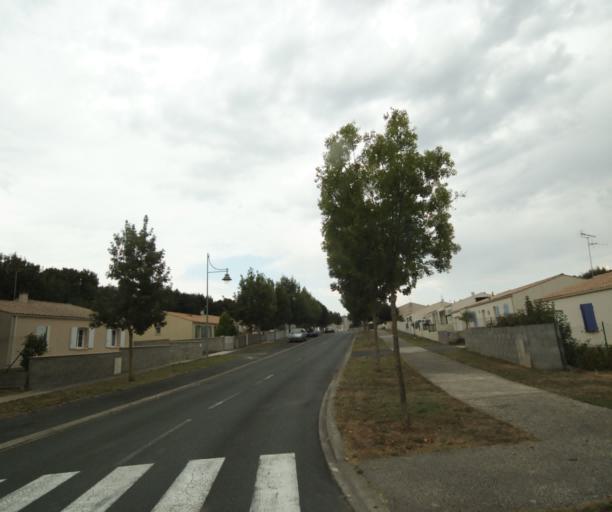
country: FR
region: Poitou-Charentes
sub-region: Departement de la Charente-Maritime
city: Tonnay-Charente
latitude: 45.9474
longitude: -0.8959
